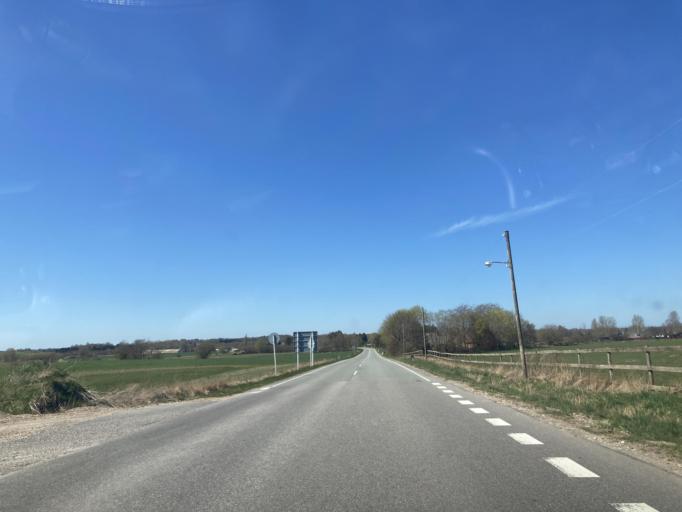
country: DK
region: Capital Region
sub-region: Gribskov Kommune
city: Helsinge
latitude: 56.0009
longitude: 12.2581
